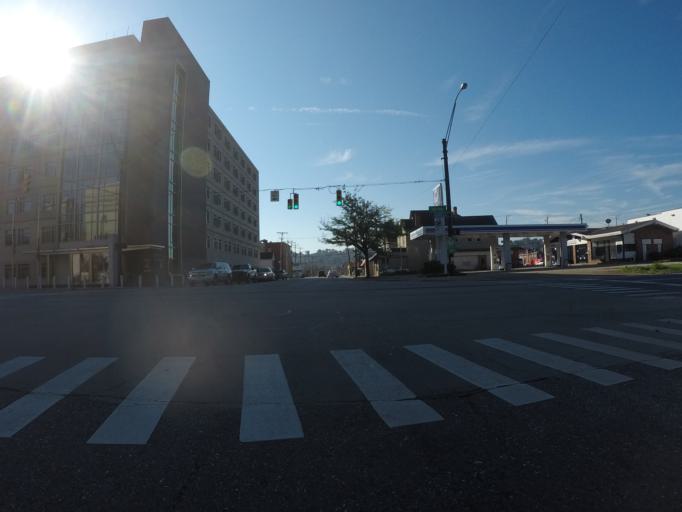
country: US
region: West Virginia
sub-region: Cabell County
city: Huntington
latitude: 38.4192
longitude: -82.4453
